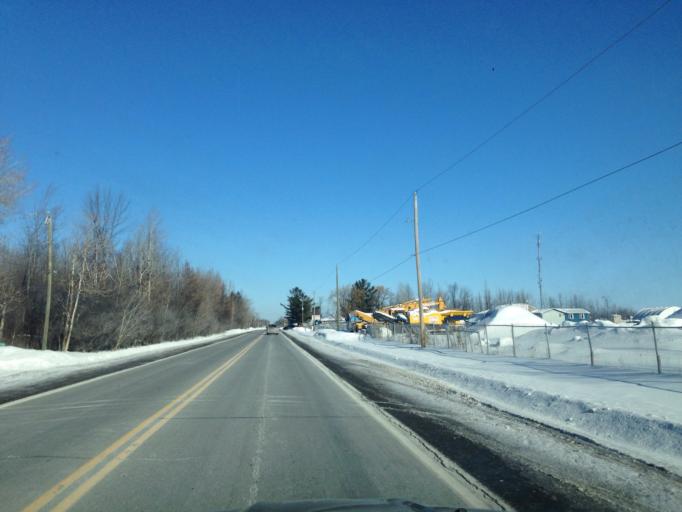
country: CA
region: Ontario
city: Clarence-Rockland
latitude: 45.3401
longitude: -75.4407
